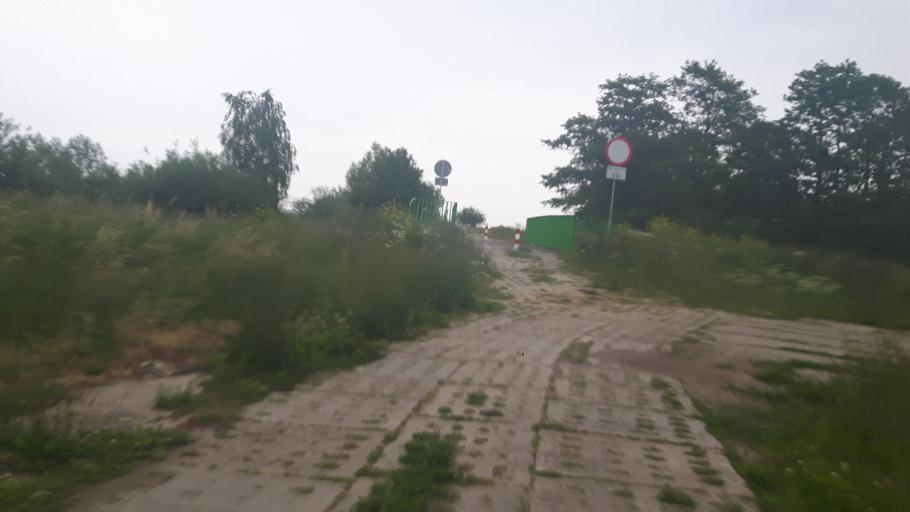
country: PL
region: Warmian-Masurian Voivodeship
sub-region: Powiat elblaski
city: Tolkmicko
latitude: 54.2978
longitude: 19.4637
